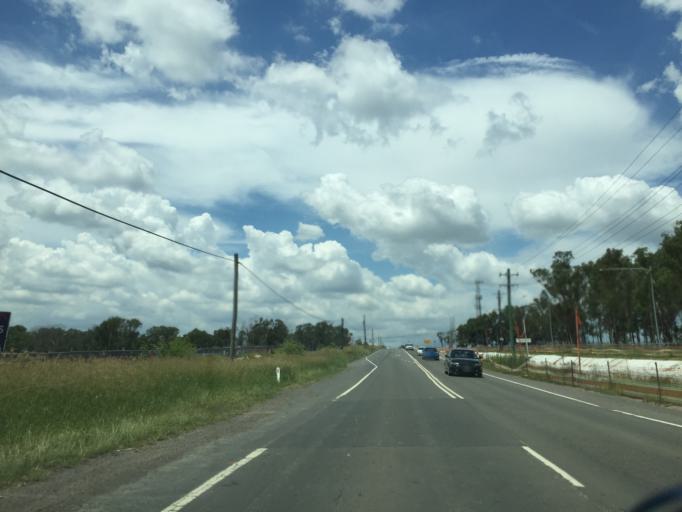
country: AU
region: New South Wales
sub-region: Blacktown
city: Hassall Grove
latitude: -33.7100
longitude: 150.8409
